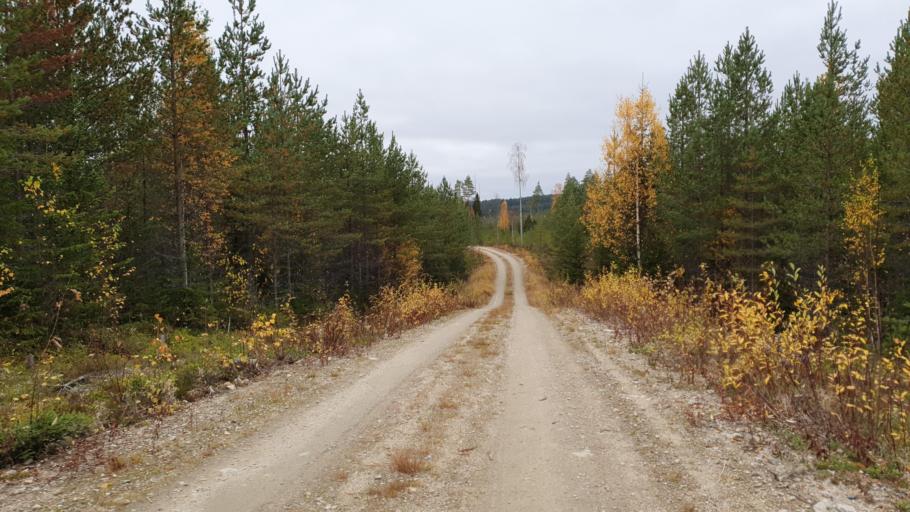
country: FI
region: Kainuu
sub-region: Kehys-Kainuu
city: Kuhmo
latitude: 64.4493
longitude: 29.6124
